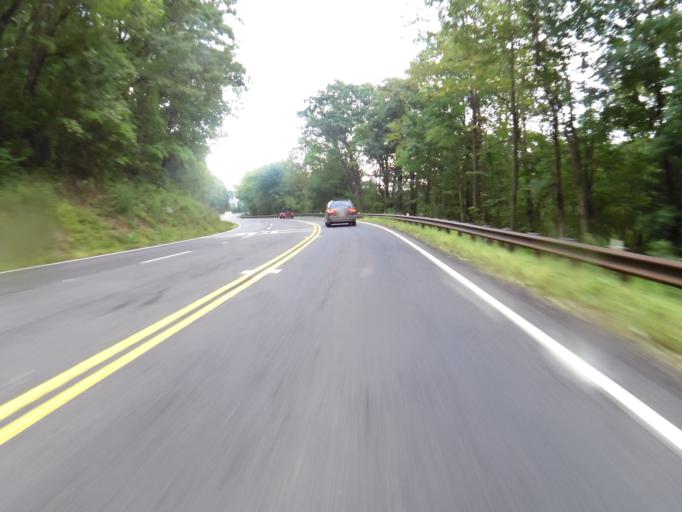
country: US
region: Virginia
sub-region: Page County
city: Luray
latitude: 38.6623
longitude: -78.3072
